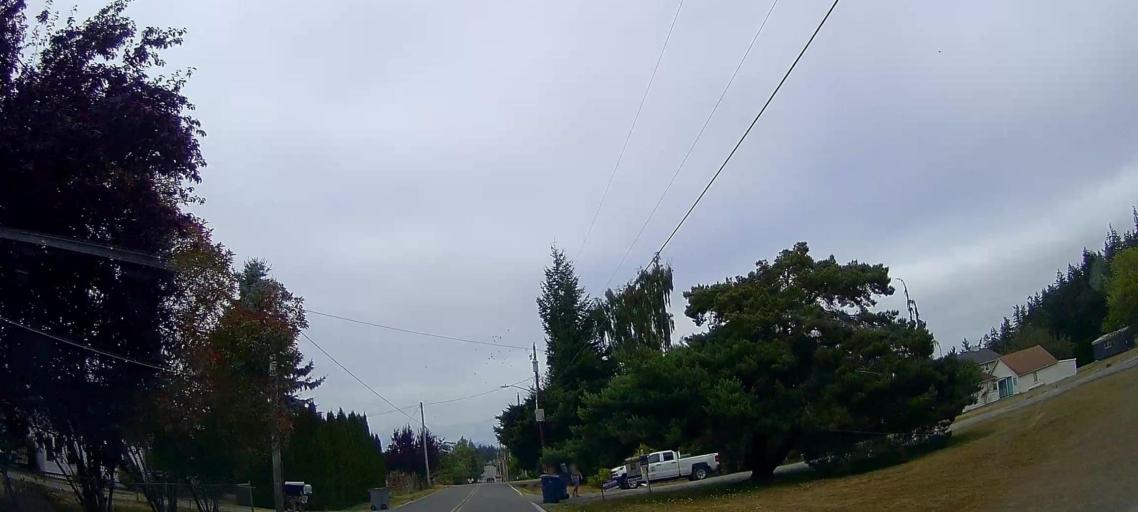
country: US
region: Washington
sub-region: Skagit County
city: Anacortes
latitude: 48.4857
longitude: -122.6251
